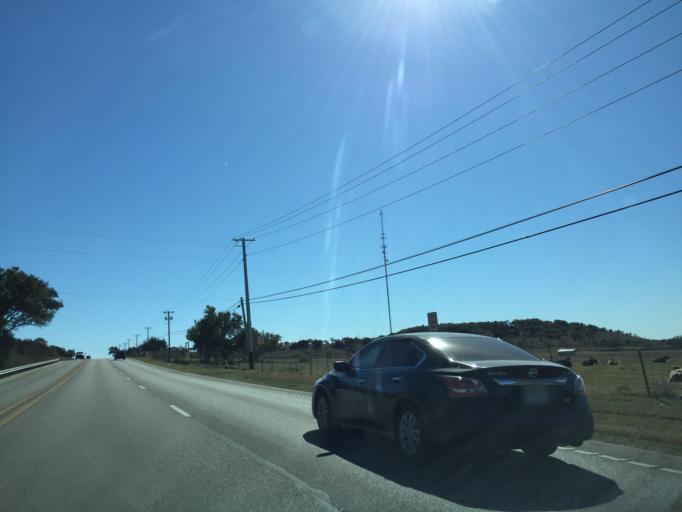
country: US
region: Texas
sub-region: Comal County
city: Canyon Lake
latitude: 29.7852
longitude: -98.3267
